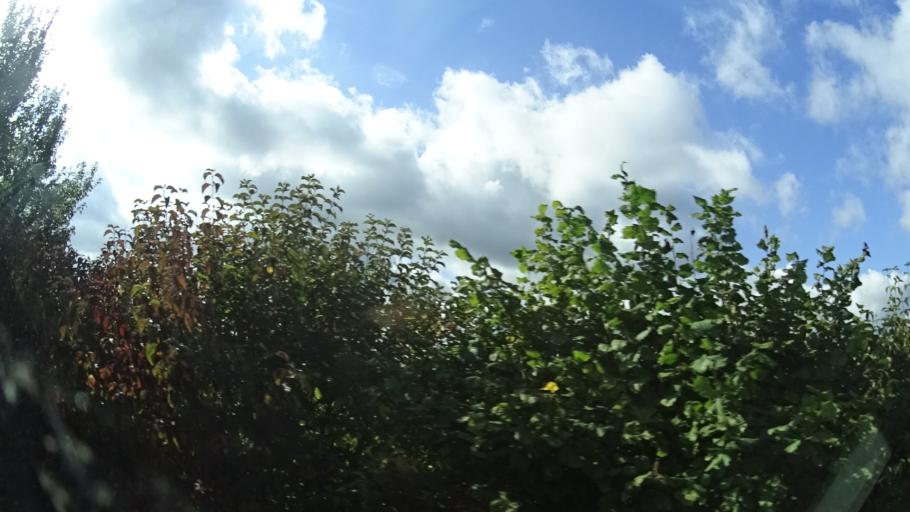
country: DE
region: Bavaria
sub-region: Regierungsbezirk Unterfranken
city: Biebelried
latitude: 49.7204
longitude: 10.0829
